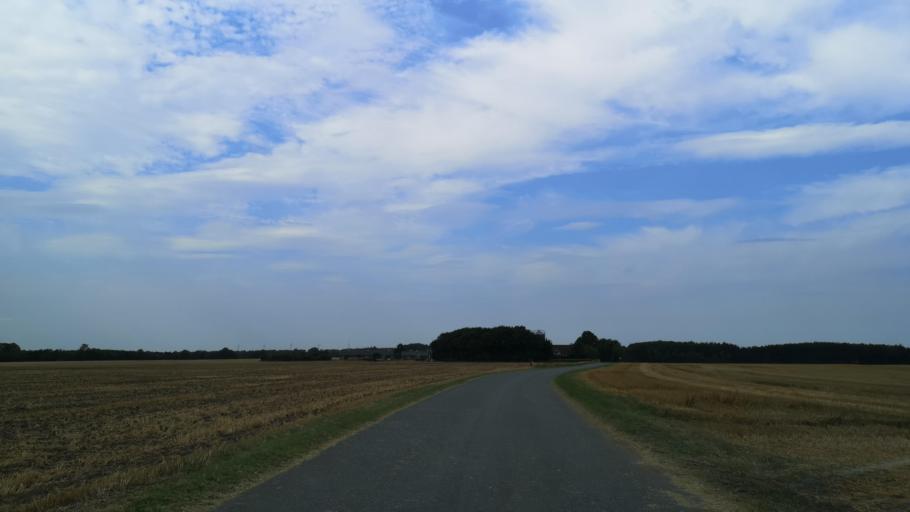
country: DK
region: Central Jutland
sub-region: Ringkobing-Skjern Kommune
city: Videbaek
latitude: 56.0774
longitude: 8.6831
